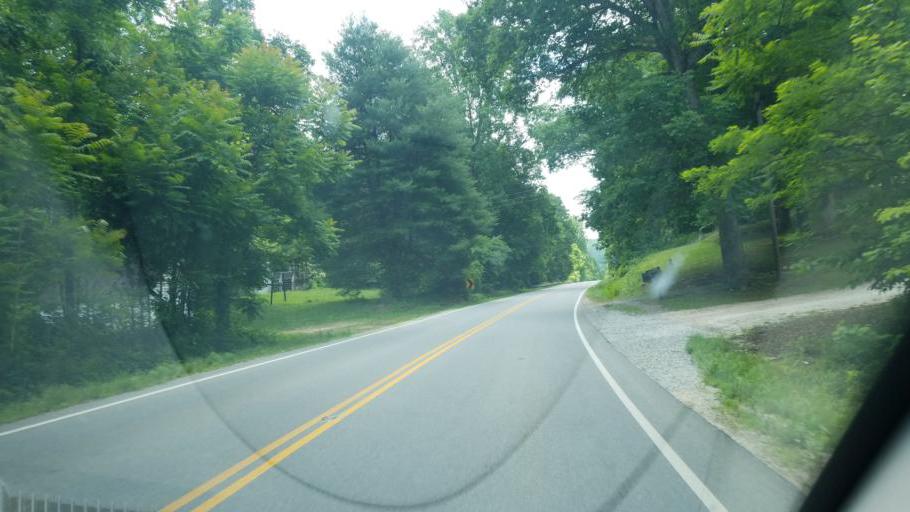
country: US
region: Virginia
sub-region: Appomattox County
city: Appomattox
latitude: 37.5468
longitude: -78.8313
